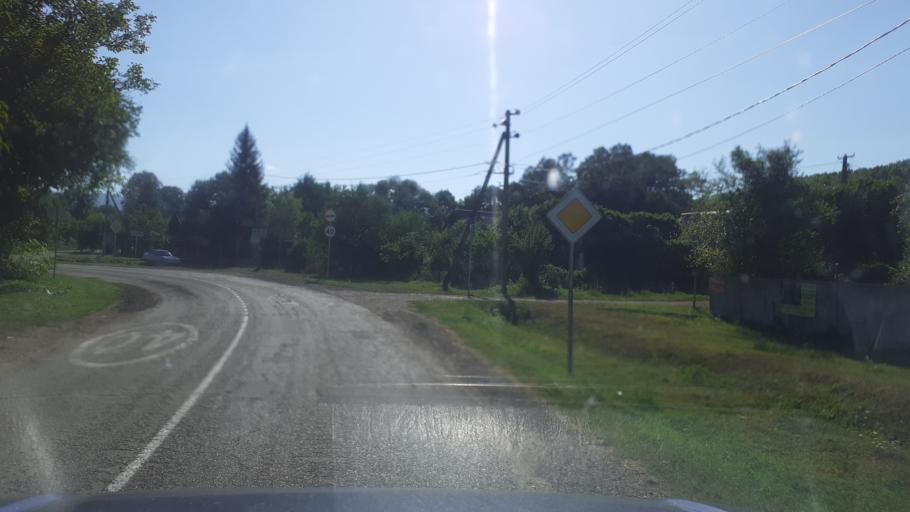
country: RU
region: Krasnodarskiy
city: Azovskaya
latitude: 44.7477
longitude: 38.5486
